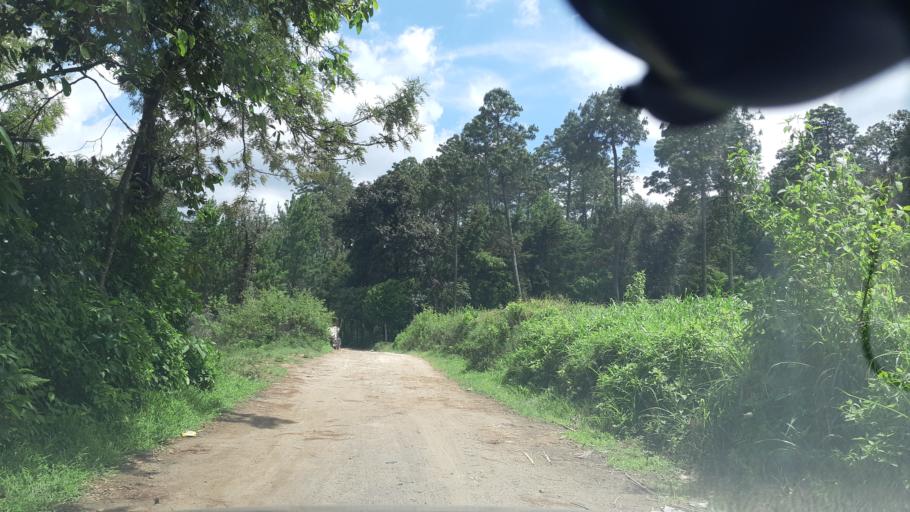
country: GT
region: Chimaltenango
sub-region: Municipio de Chimaltenango
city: Chimaltenango
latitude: 14.6596
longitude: -90.8473
